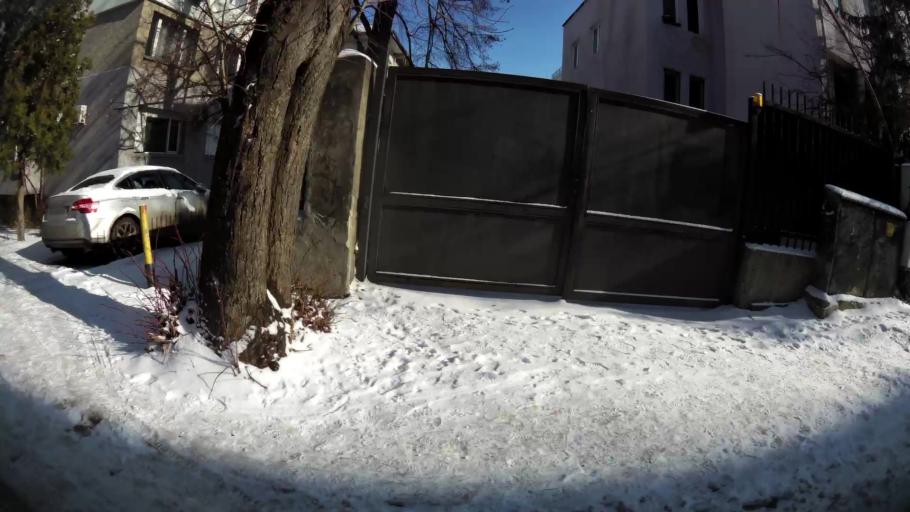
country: BG
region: Sofia-Capital
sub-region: Stolichna Obshtina
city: Sofia
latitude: 42.6755
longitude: 23.3299
